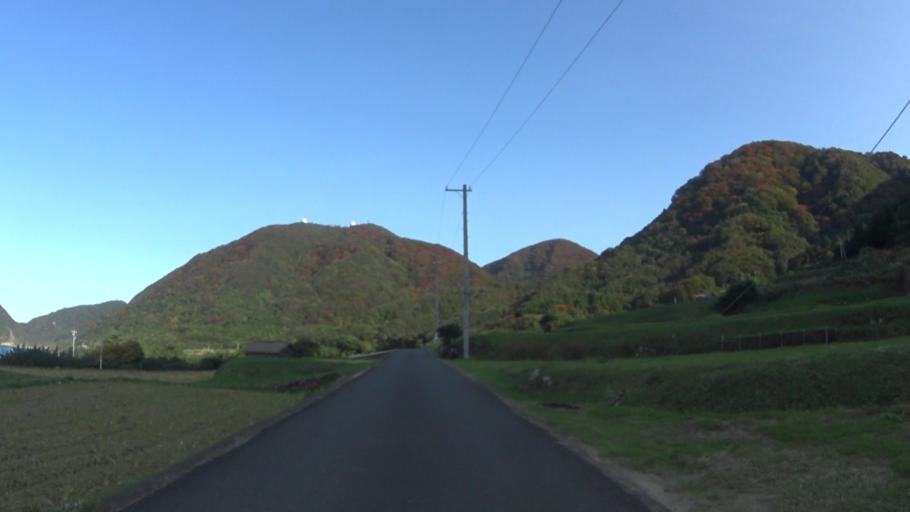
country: JP
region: Kyoto
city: Miyazu
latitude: 35.7620
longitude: 135.2015
